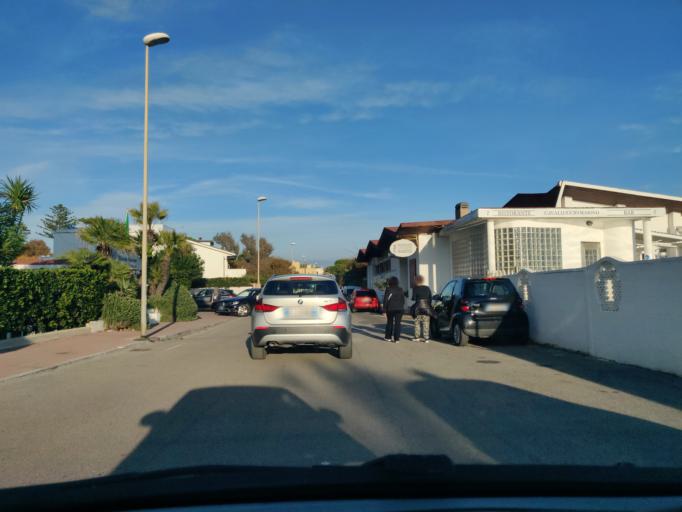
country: IT
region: Latium
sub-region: Citta metropolitana di Roma Capitale
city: Santa Marinella
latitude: 42.0311
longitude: 11.8470
